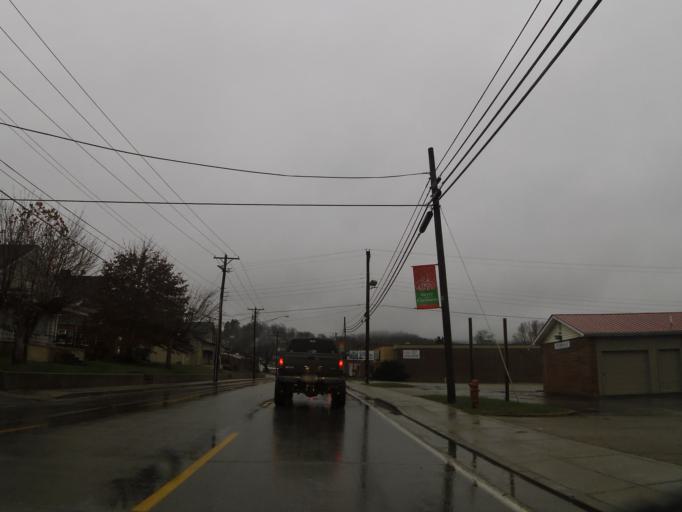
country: US
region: Kentucky
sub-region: Rockcastle County
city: Mount Vernon
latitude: 37.3573
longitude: -84.3394
